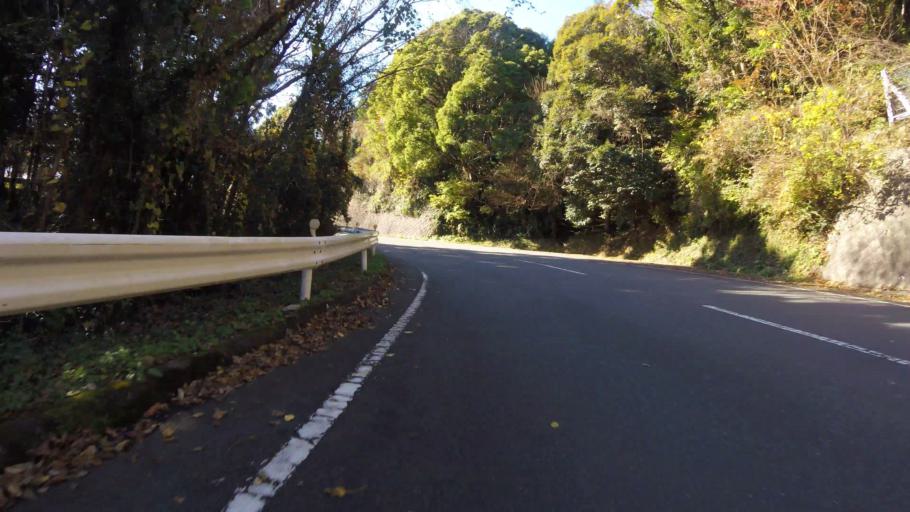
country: JP
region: Shizuoka
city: Shimoda
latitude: 34.7603
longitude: 138.9723
